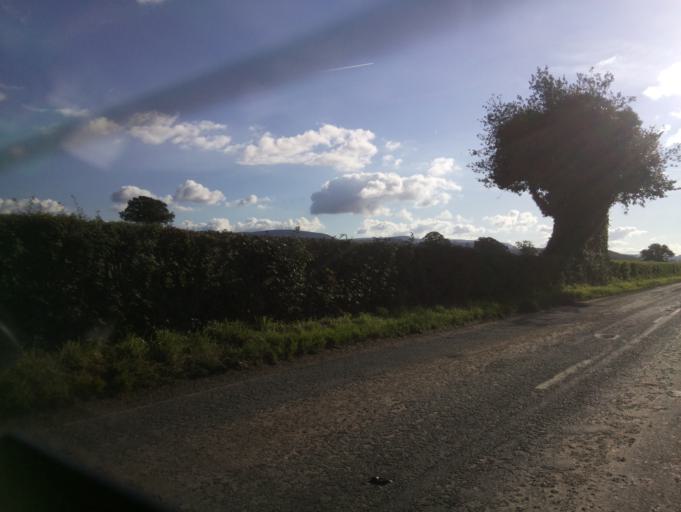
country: GB
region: England
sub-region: Herefordshire
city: Clifford
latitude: 52.0942
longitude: -3.1115
